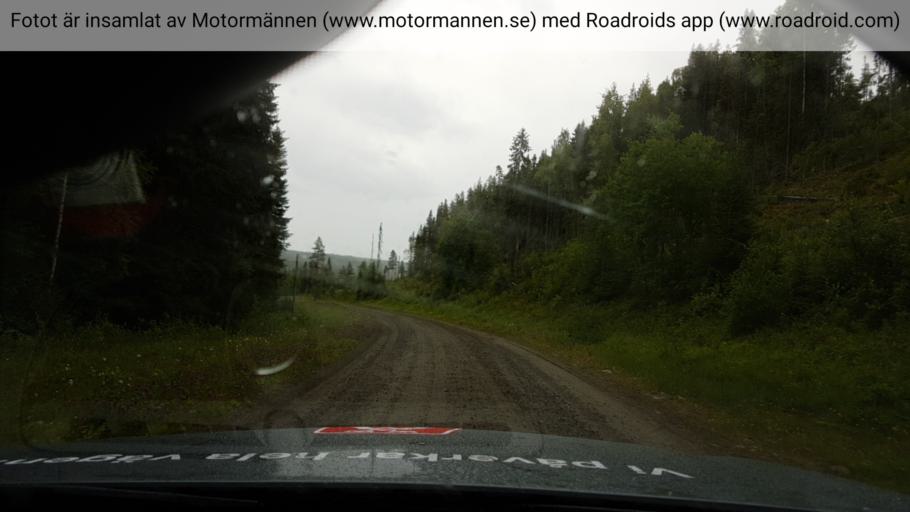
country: SE
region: Jaemtland
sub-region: Bergs Kommun
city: Hoverberg
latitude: 62.5491
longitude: 14.6932
